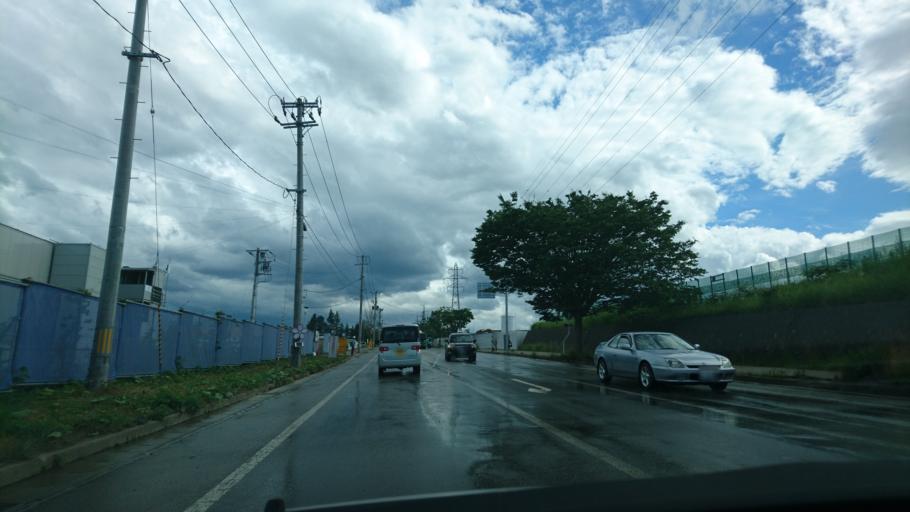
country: JP
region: Iwate
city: Hanamaki
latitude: 39.3400
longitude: 141.1287
